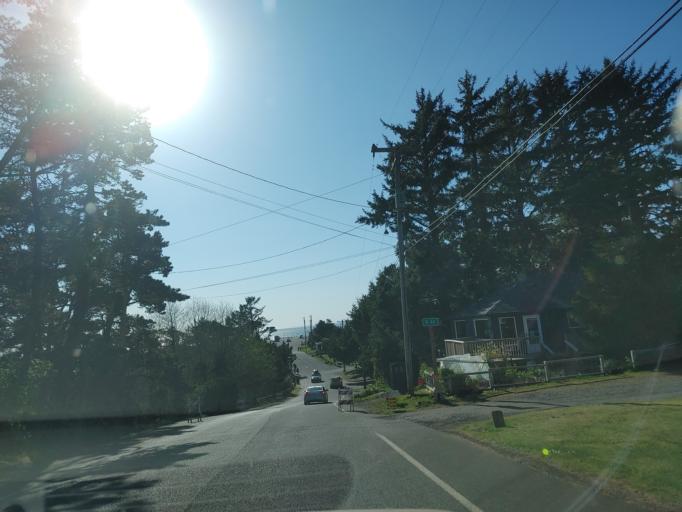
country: US
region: Oregon
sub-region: Lincoln County
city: Depoe Bay
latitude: 44.7472
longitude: -124.0611
